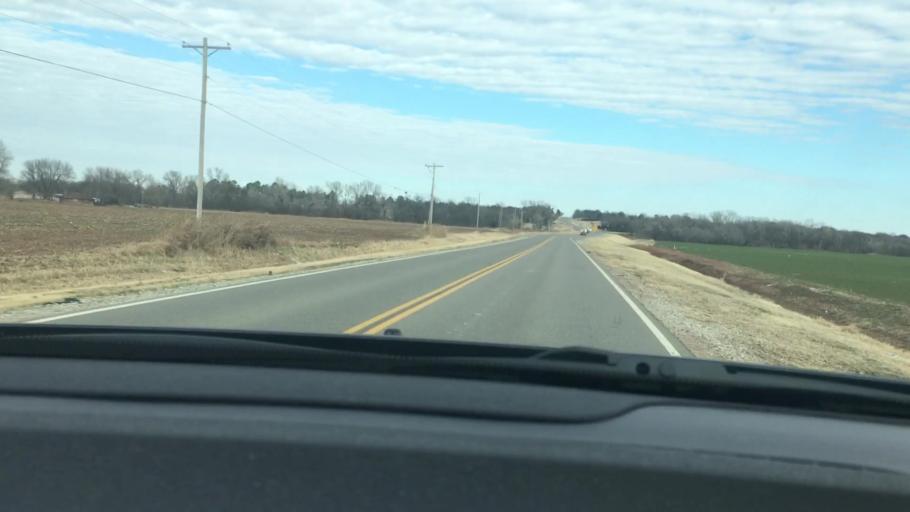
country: US
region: Oklahoma
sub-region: Garvin County
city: Pauls Valley
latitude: 34.7560
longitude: -97.2031
